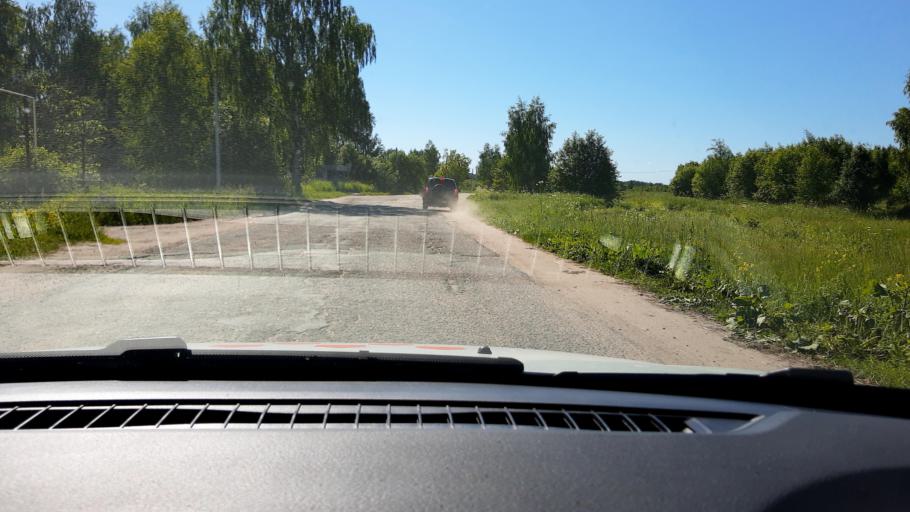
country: RU
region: Nizjnij Novgorod
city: Bor
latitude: 56.3939
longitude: 44.1090
